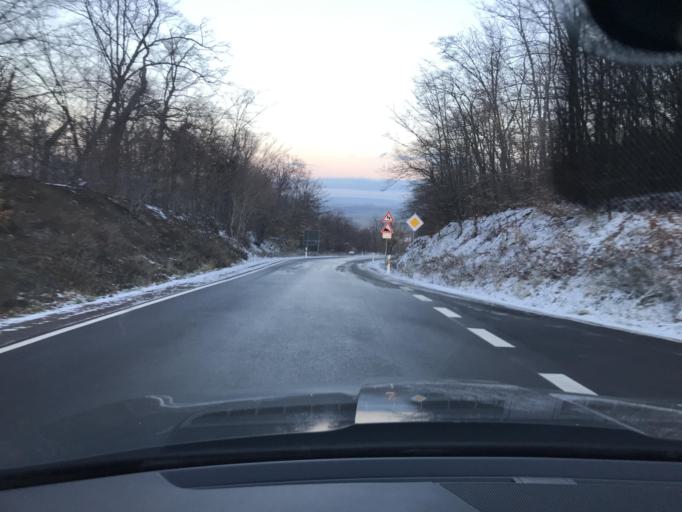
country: DE
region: Saxony-Anhalt
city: Timmenrode
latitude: 51.7446
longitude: 11.0066
